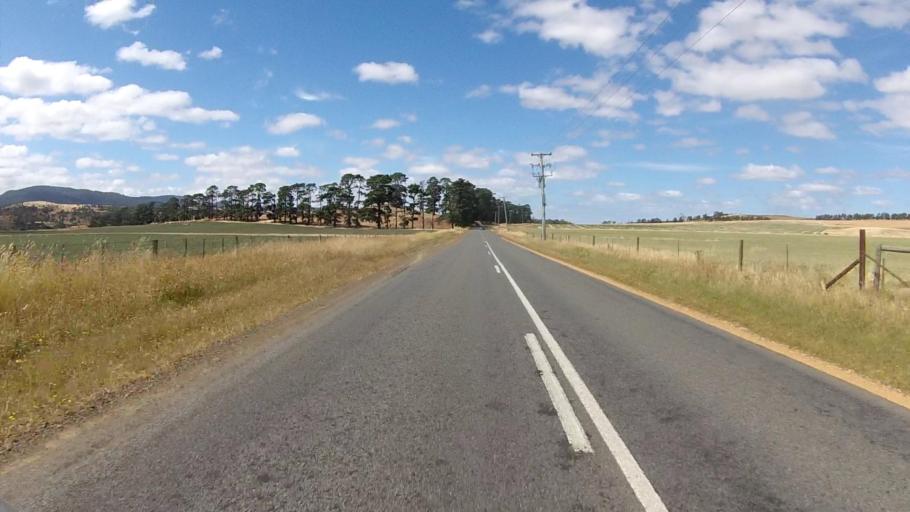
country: AU
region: Tasmania
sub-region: Sorell
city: Sorell
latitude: -42.6352
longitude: 147.4309
